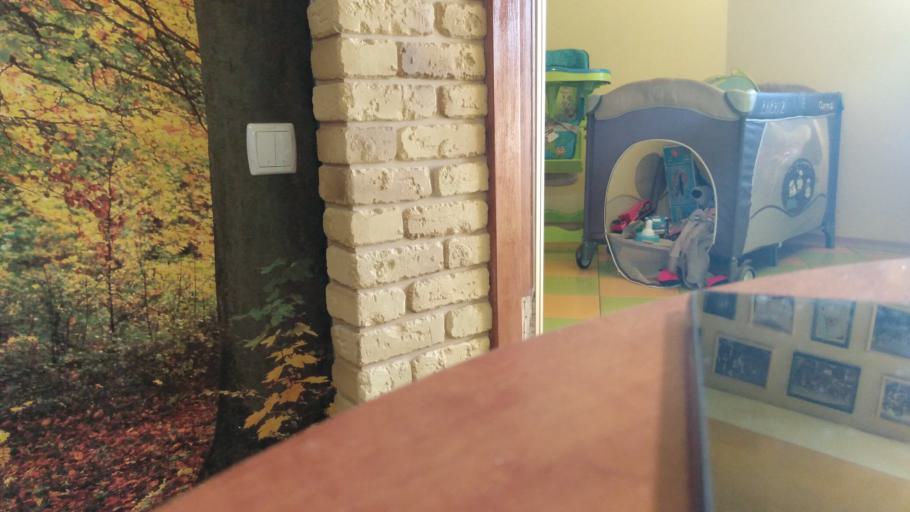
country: RU
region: Tverskaya
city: Bologoye
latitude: 57.8929
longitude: 34.2686
